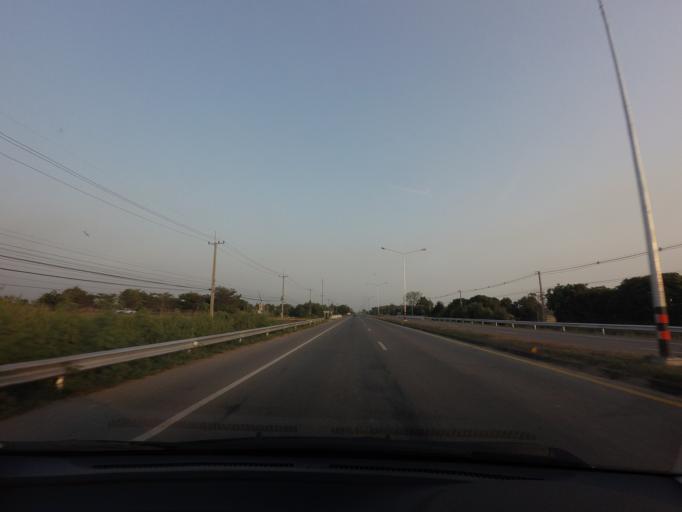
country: TH
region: Sukhothai
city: Sukhothai
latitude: 17.0185
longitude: 99.9045
